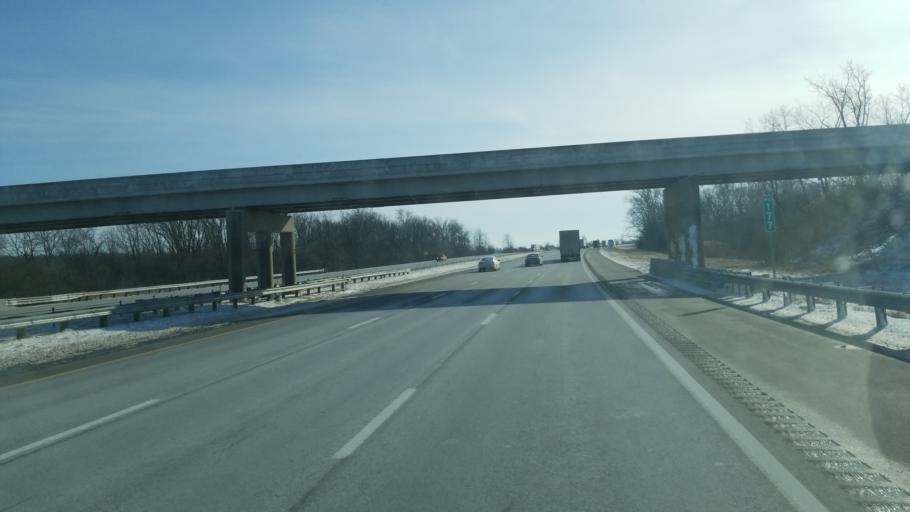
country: US
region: Ohio
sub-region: Wood County
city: Bowling Green
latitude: 41.3116
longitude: -83.6269
